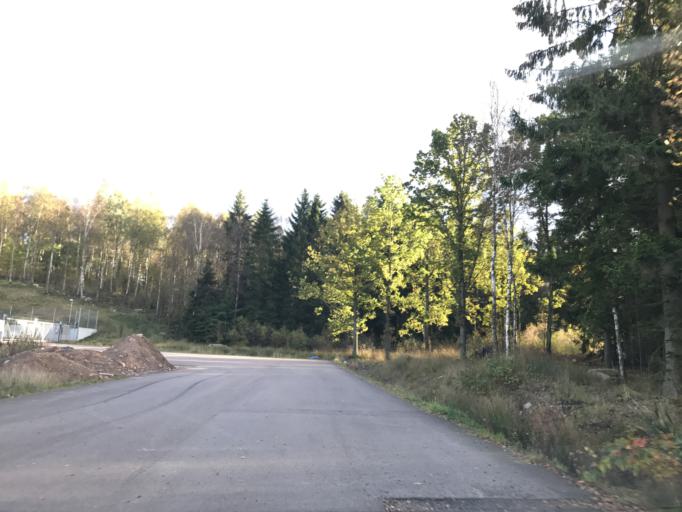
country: SE
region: Skane
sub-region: Perstorps Kommun
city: Perstorp
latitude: 56.1323
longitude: 13.3840
